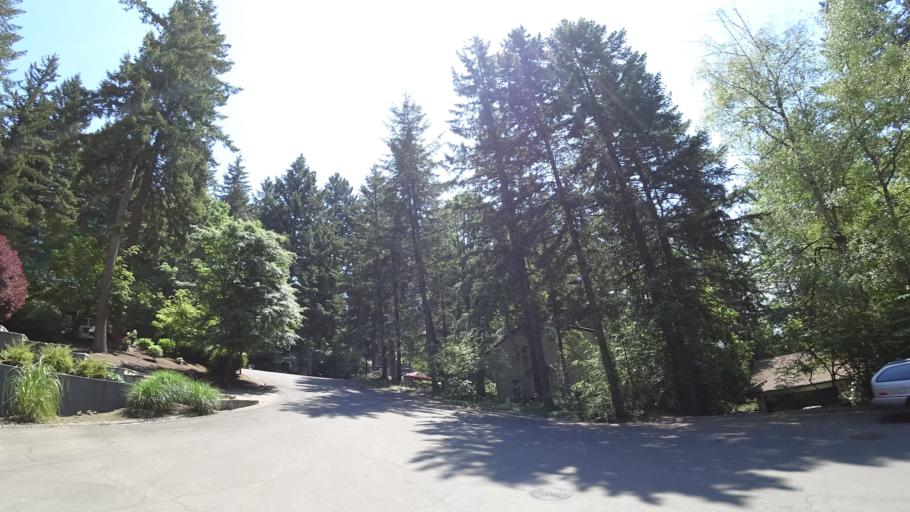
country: US
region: Oregon
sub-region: Washington County
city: Metzger
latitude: 45.4312
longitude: -122.7224
